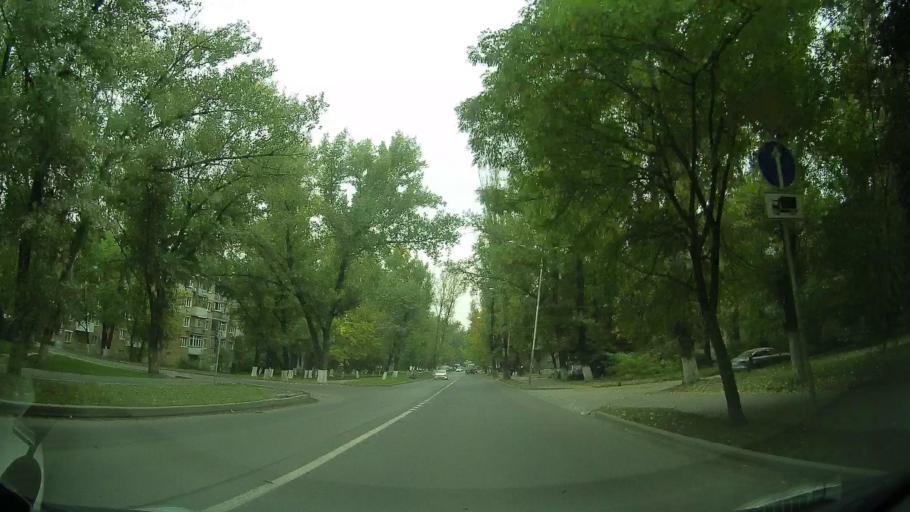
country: RU
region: Rostov
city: Severnyy
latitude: 47.2689
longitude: 39.6653
